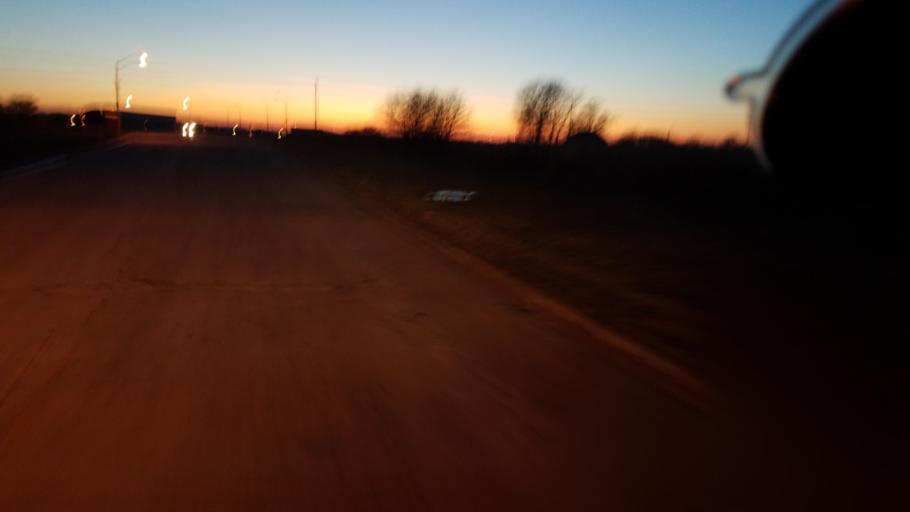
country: US
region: Illinois
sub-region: Kane County
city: Hampshire
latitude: 42.1524
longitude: -88.5139
